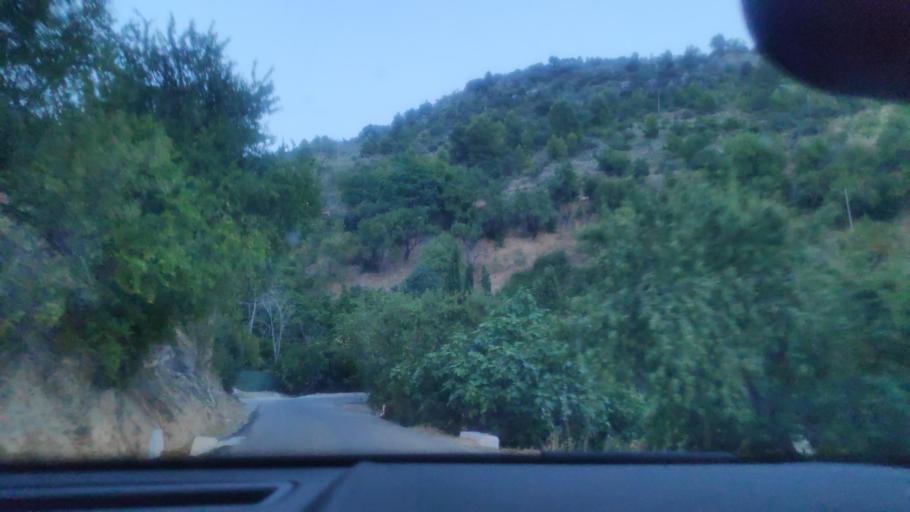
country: ES
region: Andalusia
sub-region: Provincia de Jaen
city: Torres
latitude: 37.7826
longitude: -3.5071
